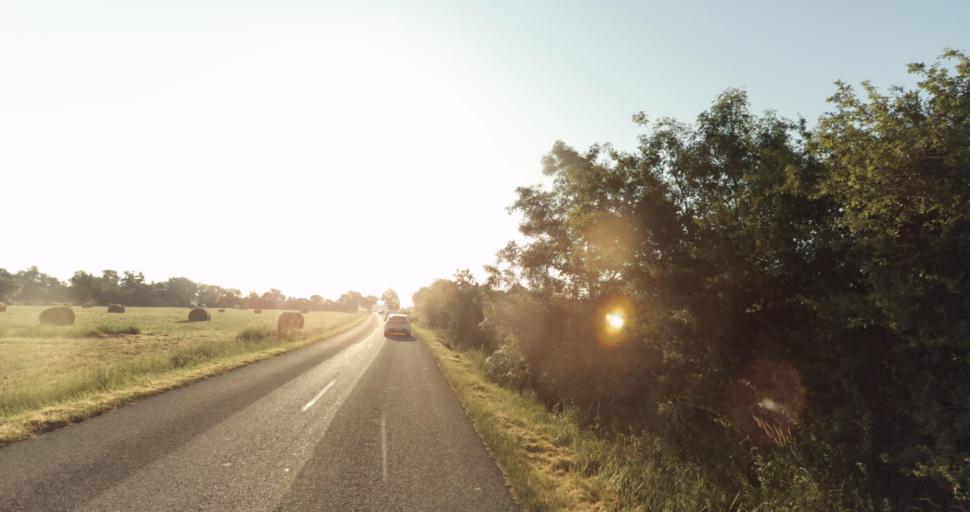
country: FR
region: Midi-Pyrenees
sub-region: Departement de la Haute-Garonne
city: Fontenilles
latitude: 43.5468
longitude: 1.1747
